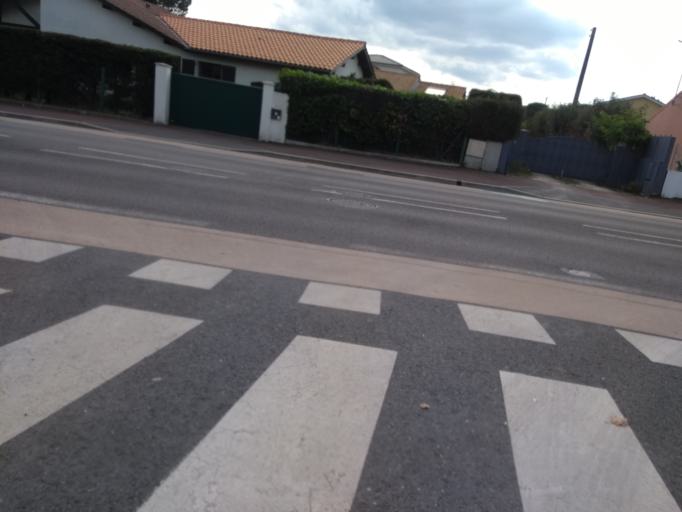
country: FR
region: Aquitaine
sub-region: Departement de la Gironde
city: Gradignan
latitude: 44.7817
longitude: -0.6219
